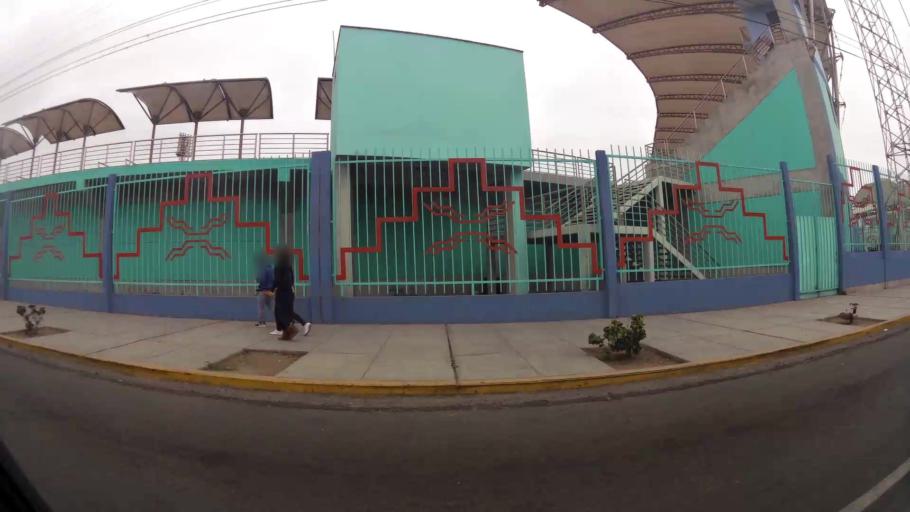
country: PE
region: La Libertad
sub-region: Provincia de Trujillo
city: Trujillo
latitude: -8.1173
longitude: -79.0170
